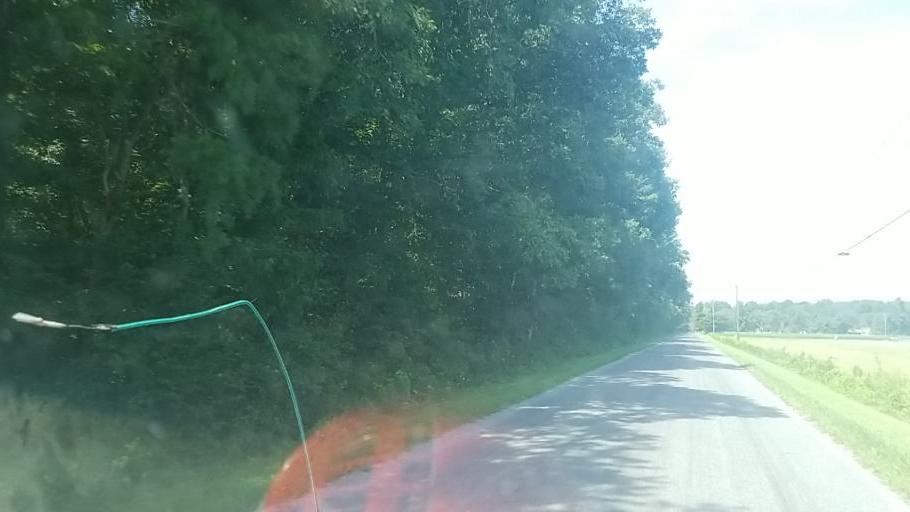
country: US
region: Maryland
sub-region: Caroline County
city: Denton
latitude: 38.8778
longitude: -75.7704
